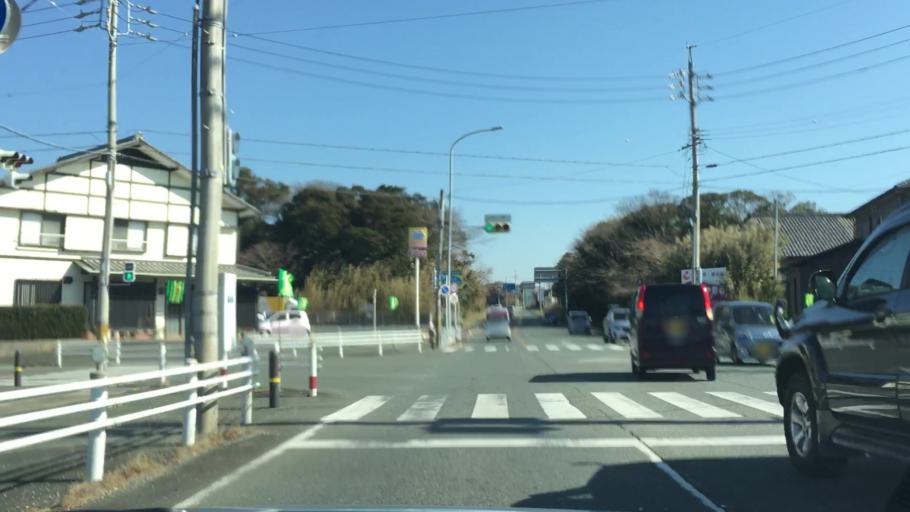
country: JP
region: Aichi
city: Tahara
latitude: 34.6629
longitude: 137.2769
